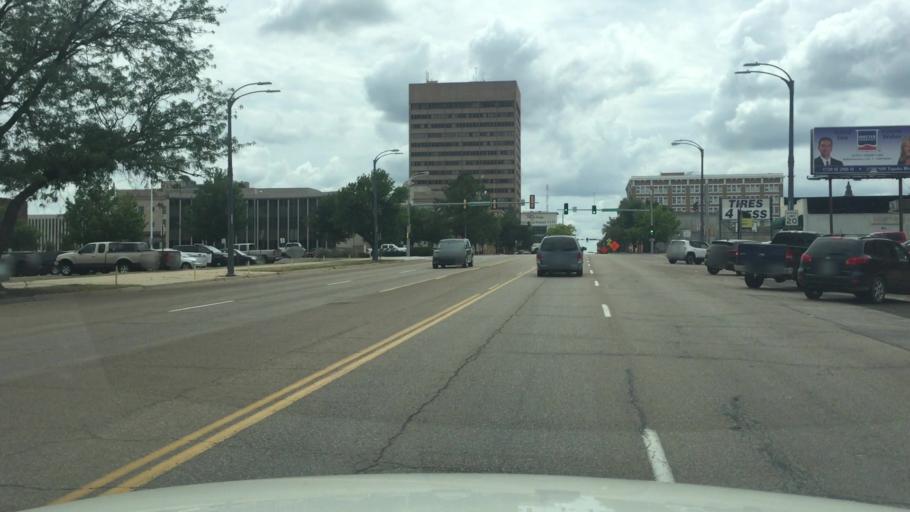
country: US
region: Kansas
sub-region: Shawnee County
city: Topeka
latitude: 39.0556
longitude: -95.6717
